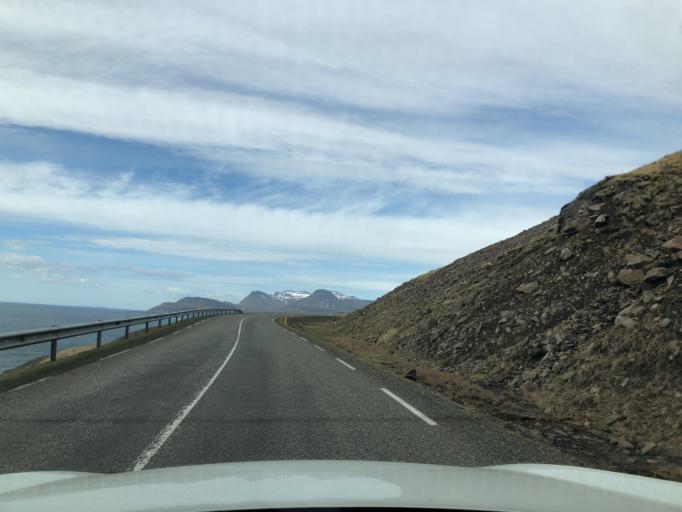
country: IS
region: East
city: Eskifjoerdur
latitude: 64.8029
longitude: -13.8708
